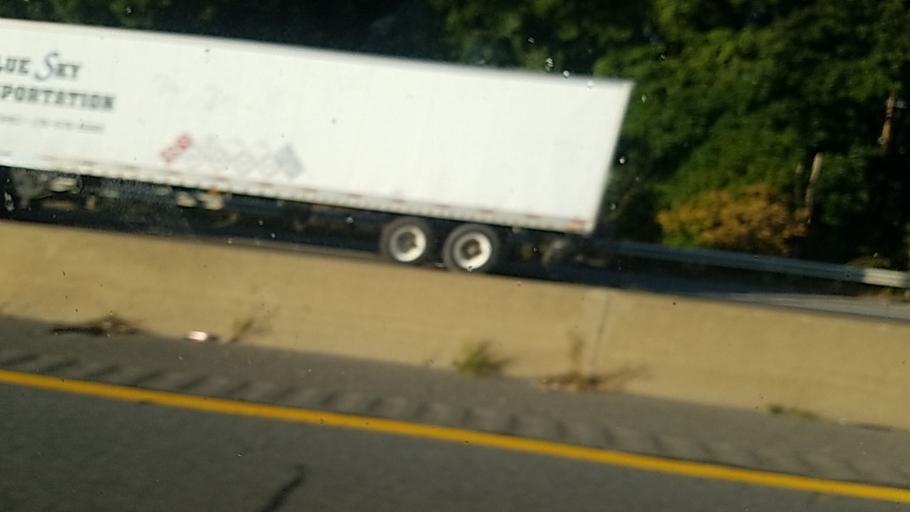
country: US
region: Ohio
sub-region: Mahoning County
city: Youngstown
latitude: 41.0978
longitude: -80.6579
